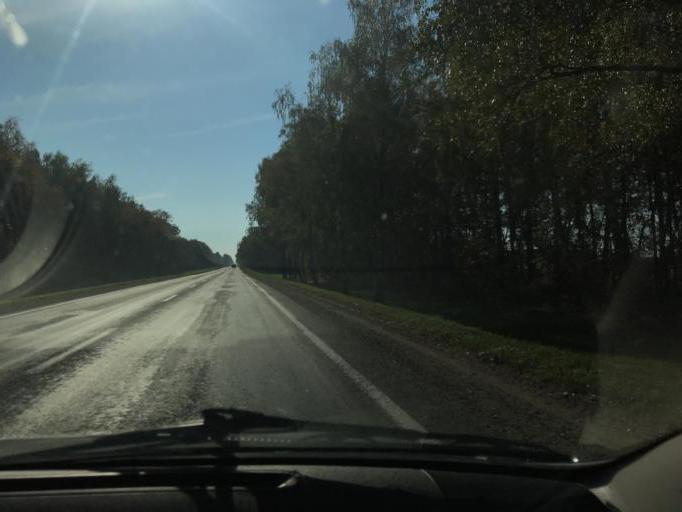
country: BY
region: Minsk
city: Salihorsk
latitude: 52.8326
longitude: 27.4659
